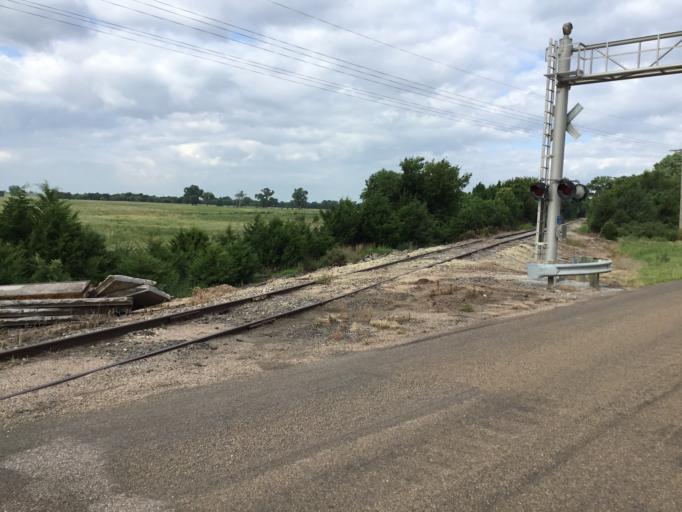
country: US
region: Kansas
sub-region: Pratt County
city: Pratt
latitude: 37.6456
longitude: -98.6479
